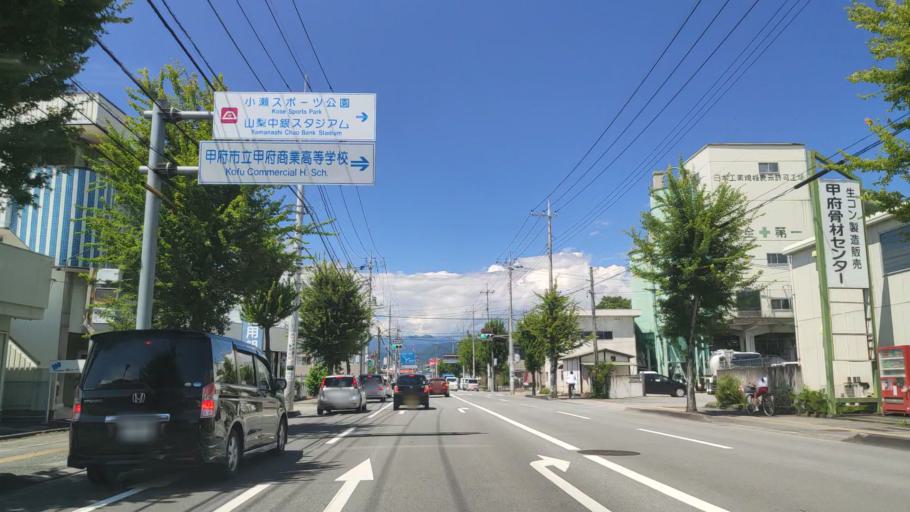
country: JP
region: Yamanashi
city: Kofu-shi
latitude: 35.6276
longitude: 138.5716
